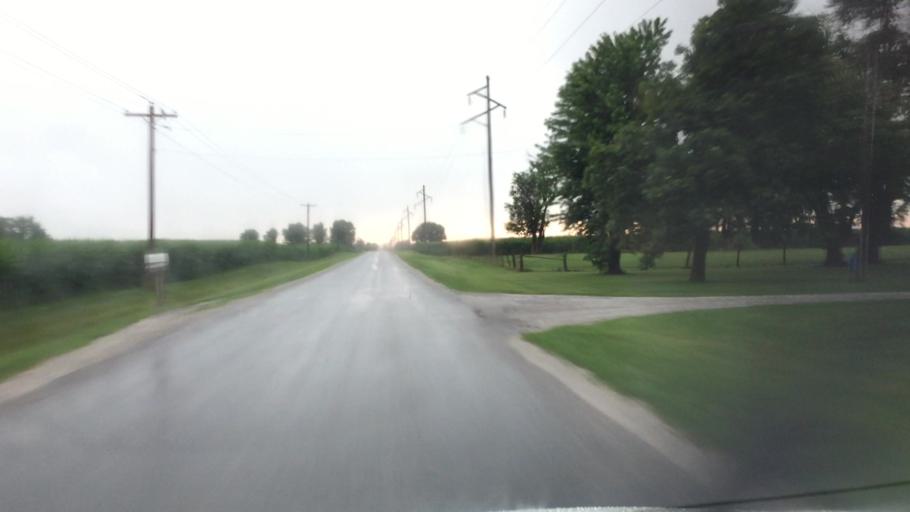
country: US
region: Illinois
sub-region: Hancock County
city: Hamilton
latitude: 40.4281
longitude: -91.2716
